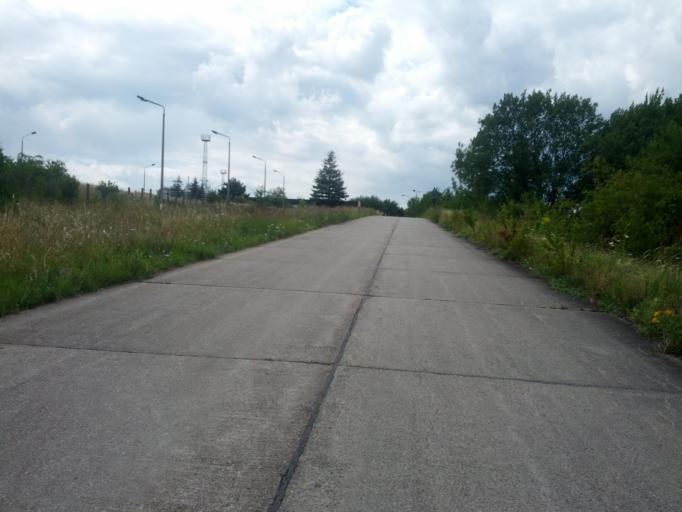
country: DE
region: Thuringia
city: Krauthausen
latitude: 51.0078
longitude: 10.2585
